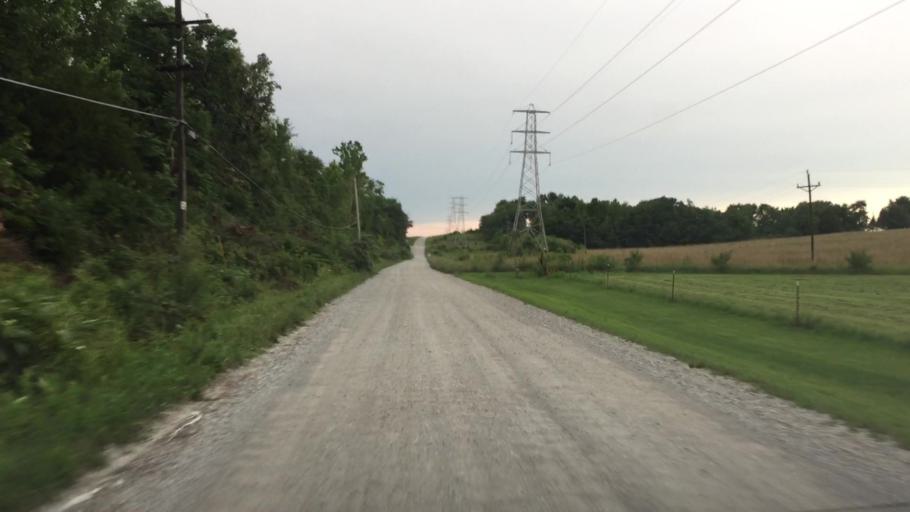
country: US
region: Illinois
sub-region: Hancock County
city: Hamilton
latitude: 40.3649
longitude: -91.3613
